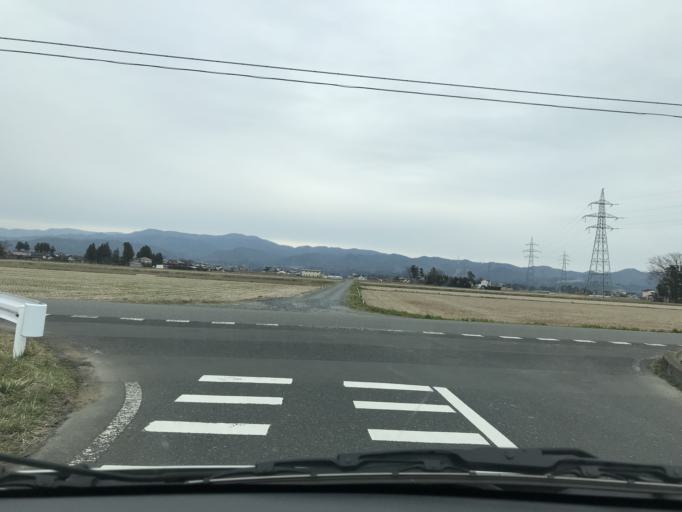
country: JP
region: Iwate
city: Mizusawa
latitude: 39.0853
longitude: 141.1443
